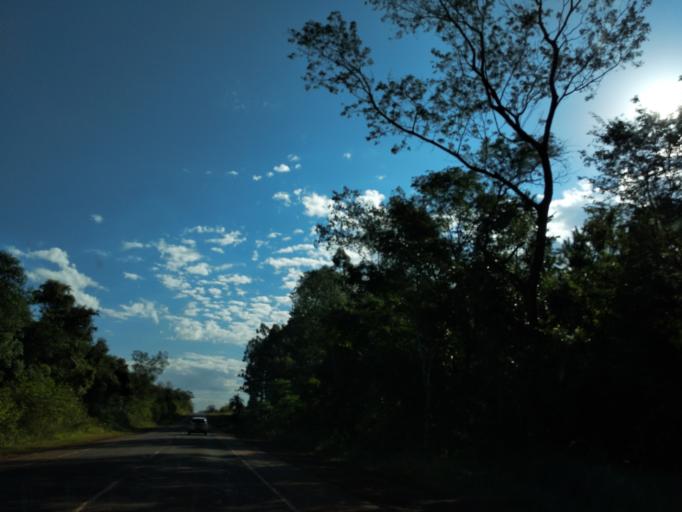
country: AR
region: Misiones
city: Ruiz de Montoya
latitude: -27.0591
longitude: -55.0194
